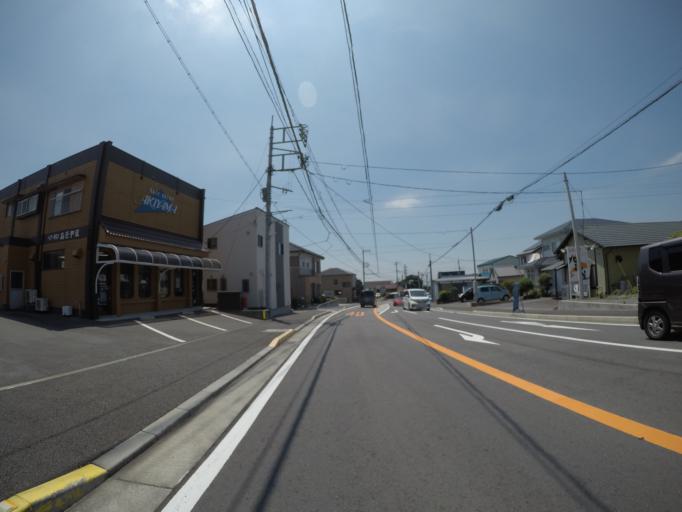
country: JP
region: Shizuoka
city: Fuji
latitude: 35.2105
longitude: 138.6866
